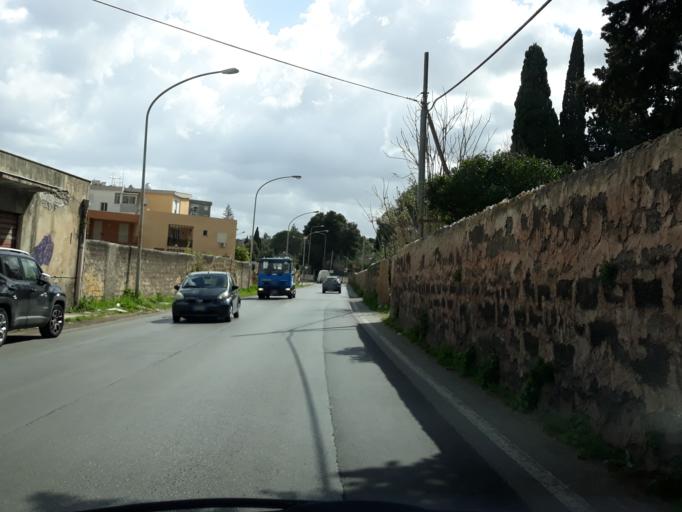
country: IT
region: Sicily
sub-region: Palermo
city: Palermo
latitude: 38.1247
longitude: 13.3166
